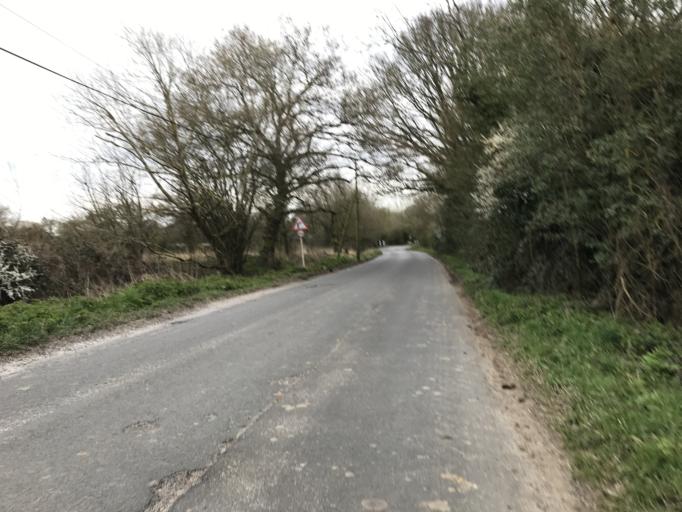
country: GB
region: England
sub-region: Essex
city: Stock
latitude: 51.6732
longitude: 0.4900
